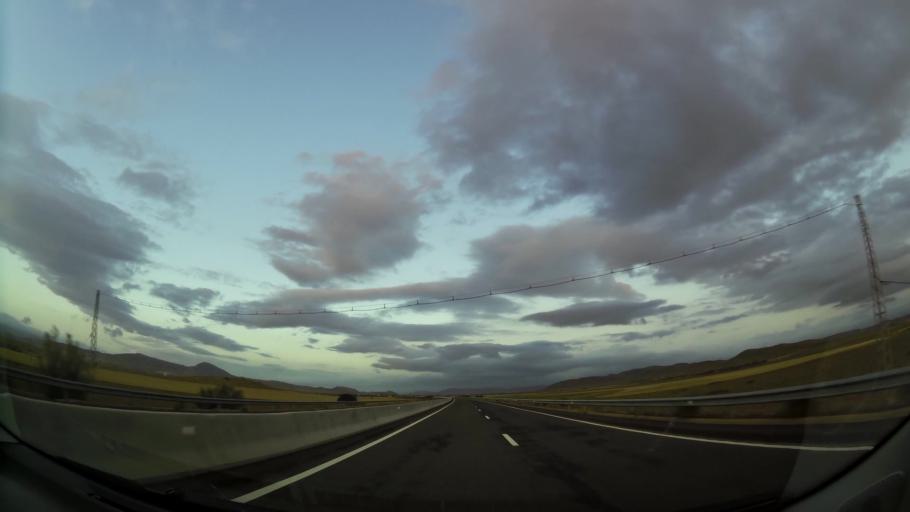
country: MA
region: Oriental
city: El Aioun
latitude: 34.5995
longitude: -2.7343
